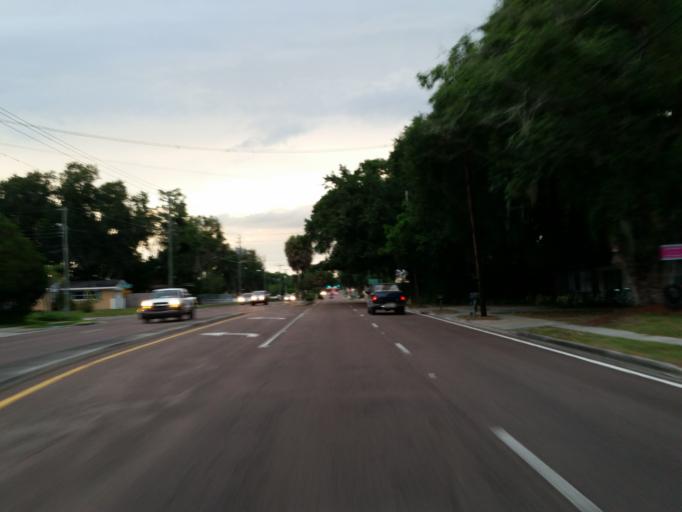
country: US
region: Florida
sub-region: Hillsborough County
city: Brandon
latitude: 27.9304
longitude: -82.2939
